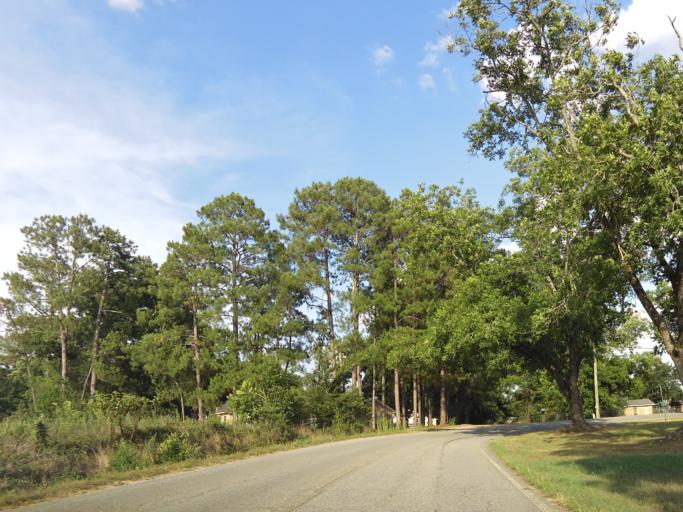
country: US
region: Georgia
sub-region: Houston County
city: Centerville
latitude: 32.7167
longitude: -83.6798
